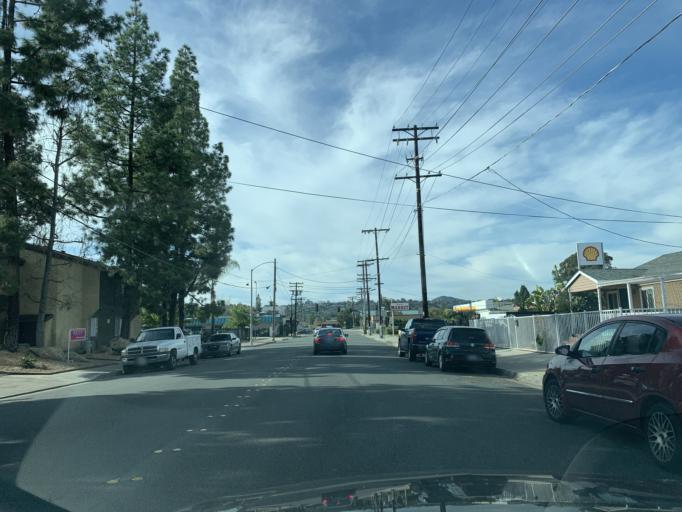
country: US
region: California
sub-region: San Diego County
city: El Cajon
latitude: 32.8009
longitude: -116.9609
